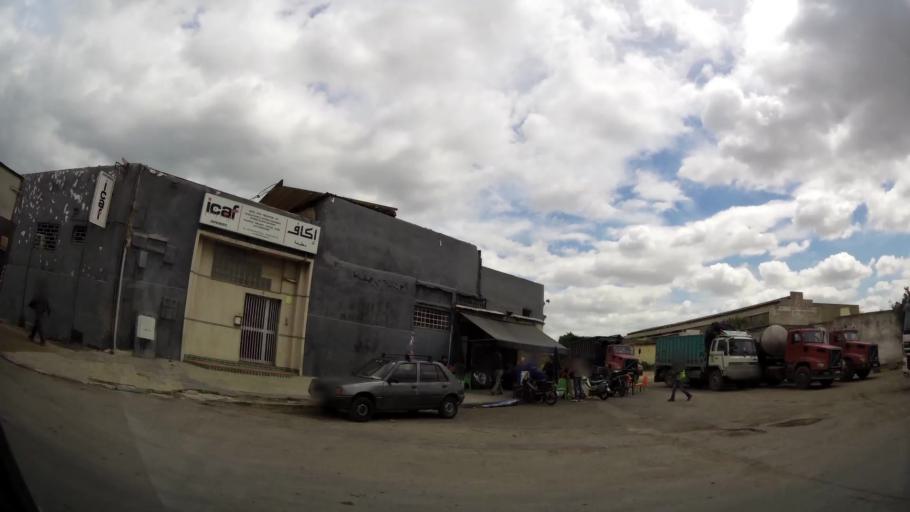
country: MA
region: Grand Casablanca
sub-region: Casablanca
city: Casablanca
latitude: 33.6078
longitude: -7.5640
